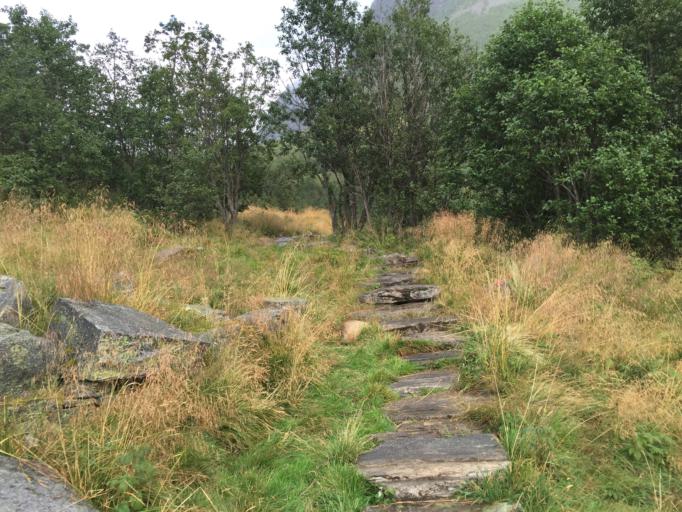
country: NO
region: More og Romsdal
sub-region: Norddal
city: Valldal
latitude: 62.1024
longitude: 7.2216
